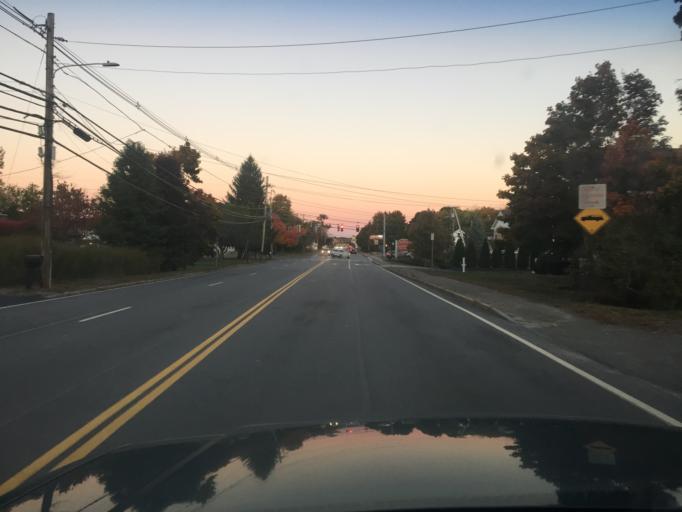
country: US
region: Massachusetts
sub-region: Worcester County
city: Milford
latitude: 42.1490
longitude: -71.4980
